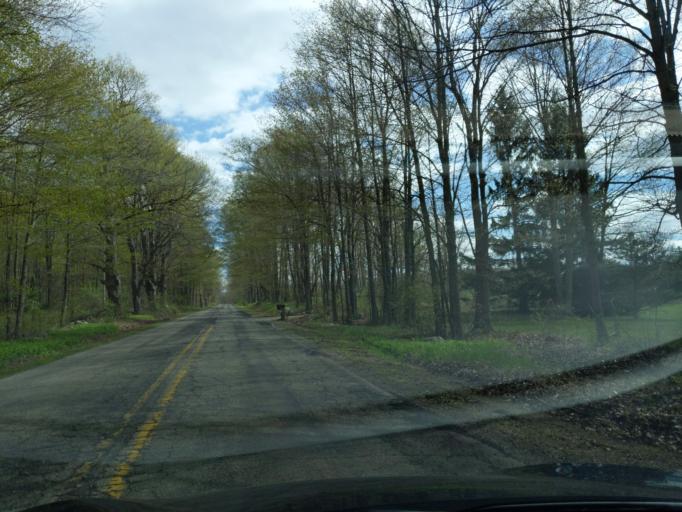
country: US
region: Michigan
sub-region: Ingham County
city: Leslie
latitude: 42.4038
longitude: -84.5268
